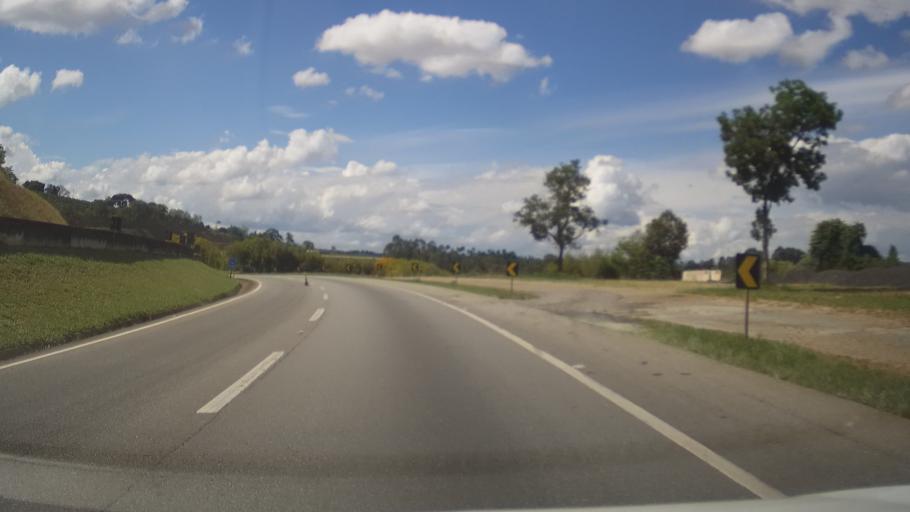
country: BR
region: Minas Gerais
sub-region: Oliveira
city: Oliveira
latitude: -20.8381
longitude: -44.8240
